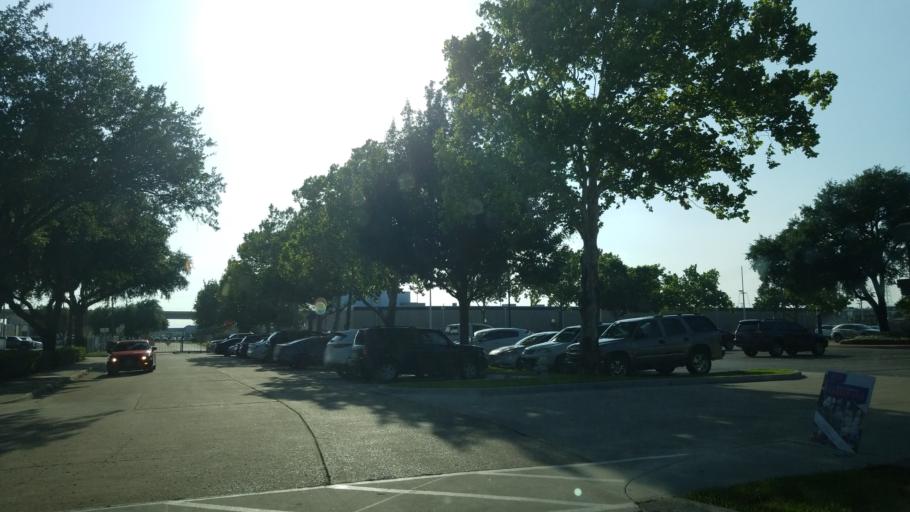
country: US
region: Texas
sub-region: Dallas County
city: Farmers Branch
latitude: 32.8789
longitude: -96.8934
